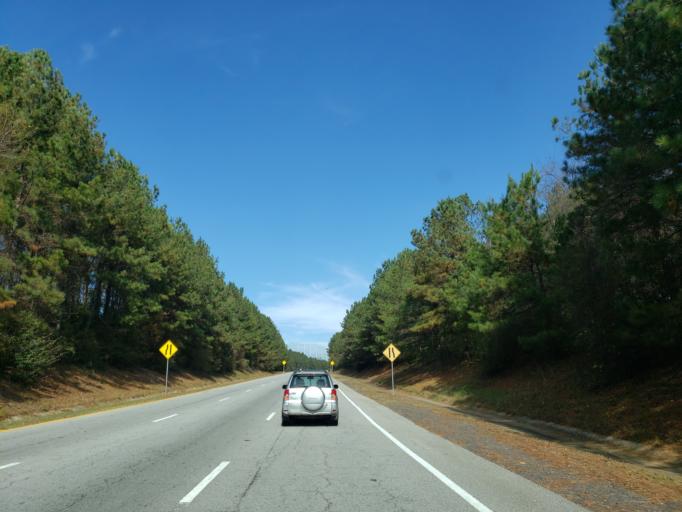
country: US
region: Georgia
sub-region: Fulton County
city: Alpharetta
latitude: 34.0391
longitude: -84.3090
